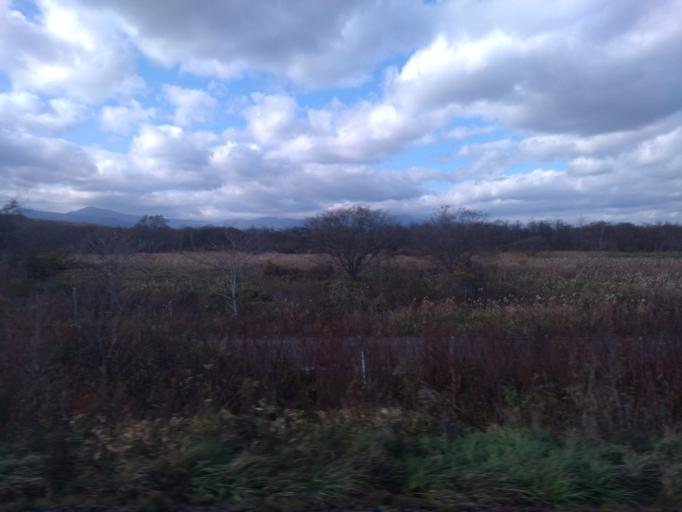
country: JP
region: Hokkaido
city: Shiraoi
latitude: 42.5027
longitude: 141.2761
